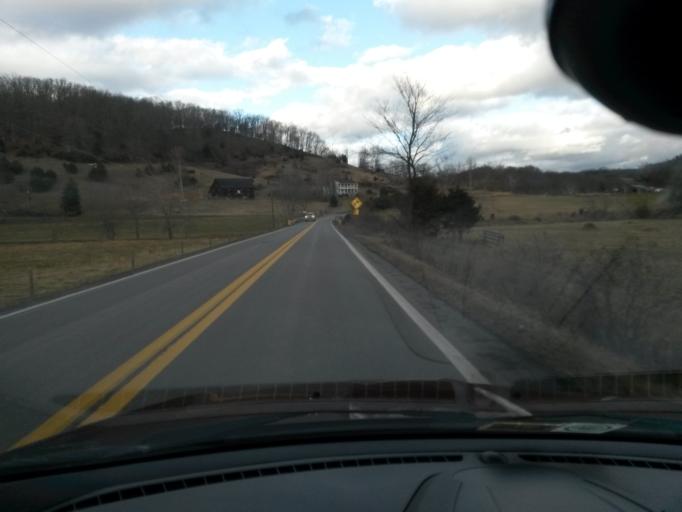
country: US
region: West Virginia
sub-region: Monroe County
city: Union
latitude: 37.5561
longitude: -80.5726
